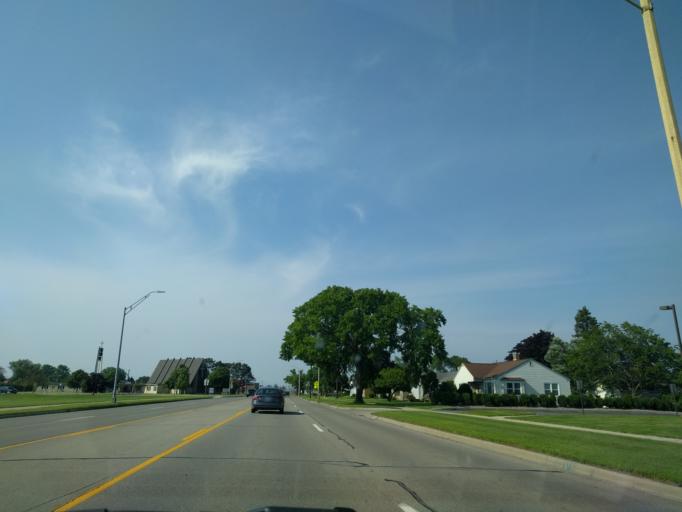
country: US
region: Michigan
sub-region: Delta County
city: Escanaba
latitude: 45.7411
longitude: -87.0798
